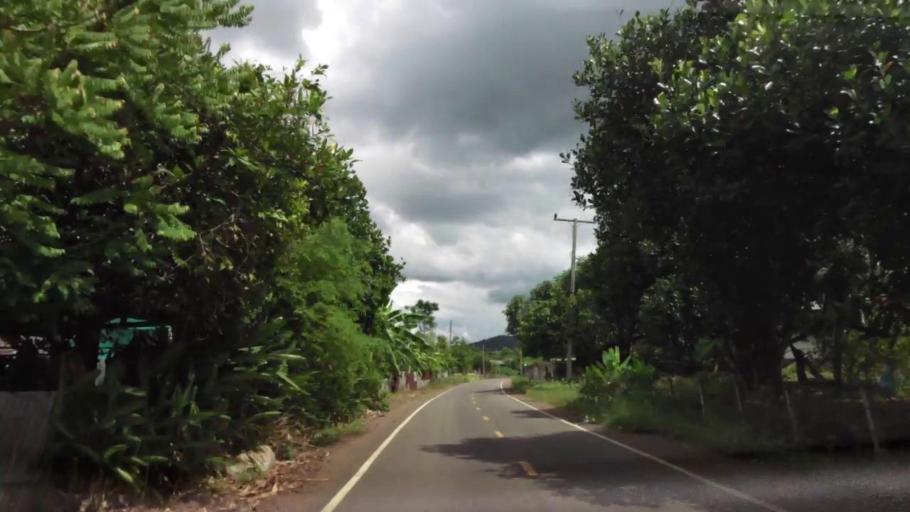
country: TH
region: Nakhon Sawan
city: Phai Sali
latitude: 15.6050
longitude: 100.6541
